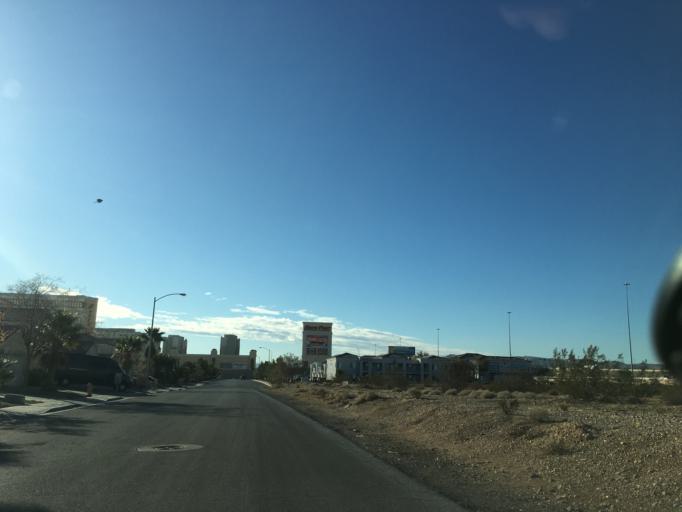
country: US
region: Nevada
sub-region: Clark County
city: Enterprise
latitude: 36.0166
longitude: -115.1788
